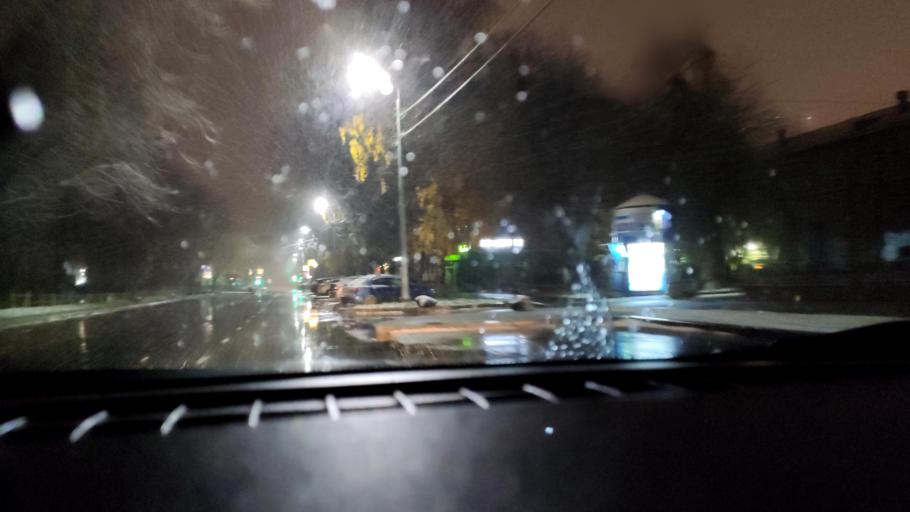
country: RU
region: Perm
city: Perm
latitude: 58.0019
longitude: 56.2534
